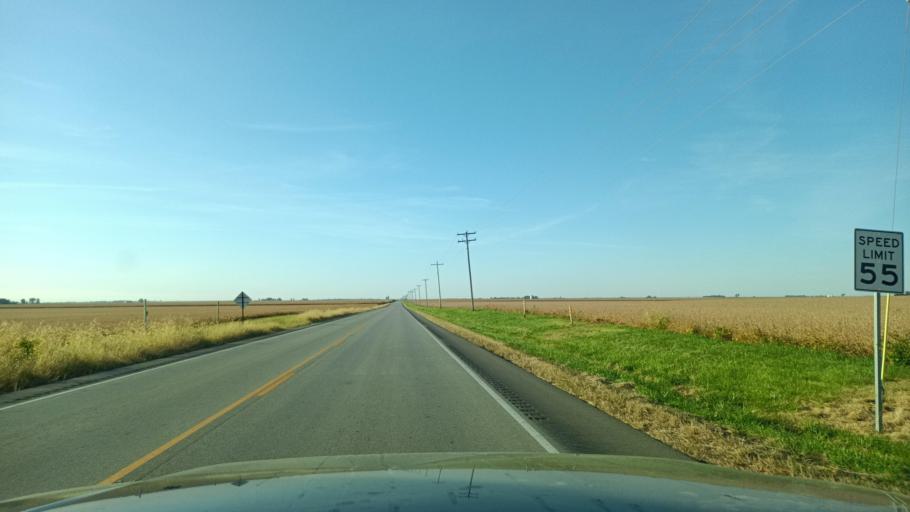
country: US
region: Illinois
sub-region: Douglas County
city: Villa Grove
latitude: 39.7901
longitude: -87.9398
